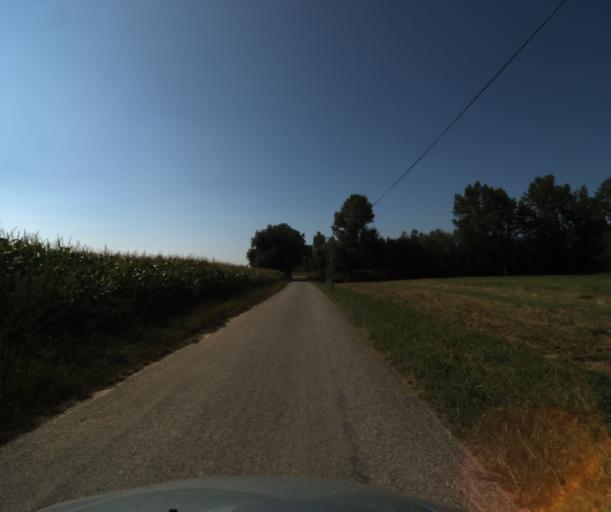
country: FR
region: Midi-Pyrenees
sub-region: Departement de la Haute-Garonne
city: Noe
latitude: 43.3676
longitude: 1.2665
